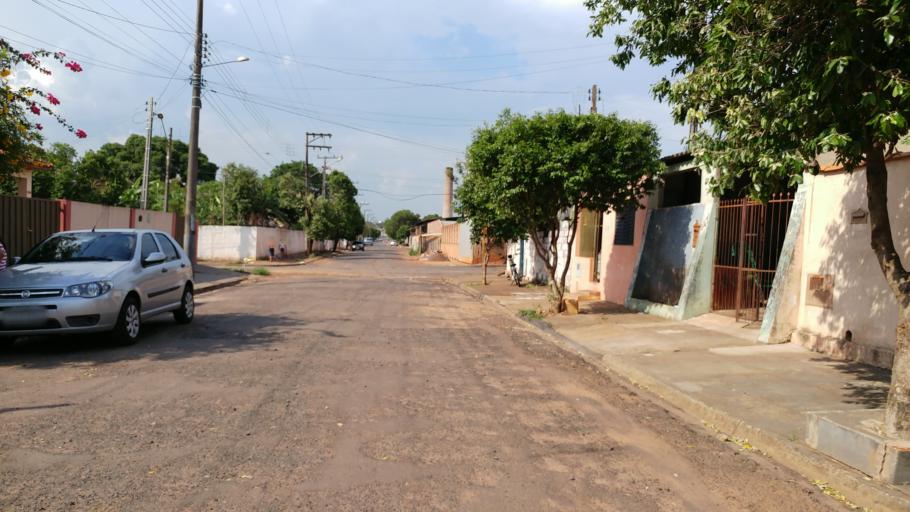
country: BR
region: Sao Paulo
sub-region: Paraguacu Paulista
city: Paraguacu Paulista
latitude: -22.4260
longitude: -50.5885
